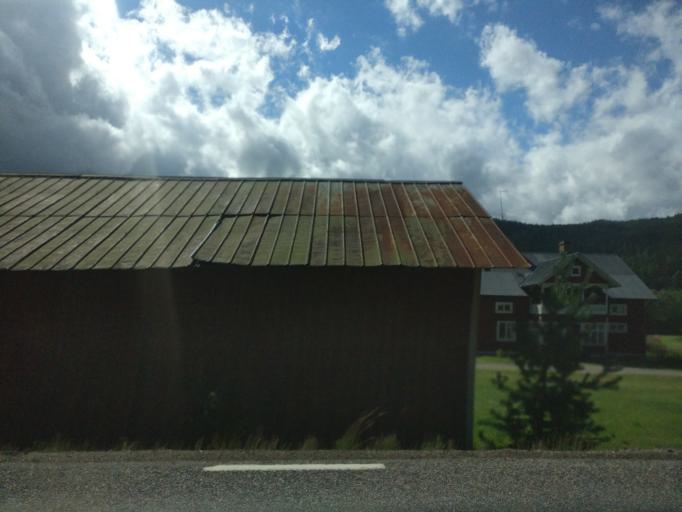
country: SE
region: Vaermland
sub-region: Hagfors Kommun
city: Ekshaerad
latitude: 60.3051
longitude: 13.3730
